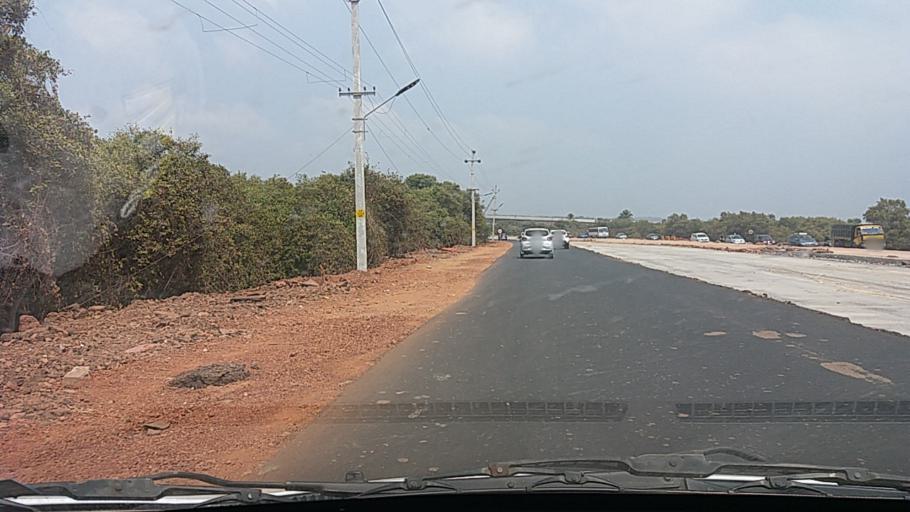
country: IN
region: Goa
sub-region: North Goa
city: Panaji
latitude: 15.4878
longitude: 73.8457
